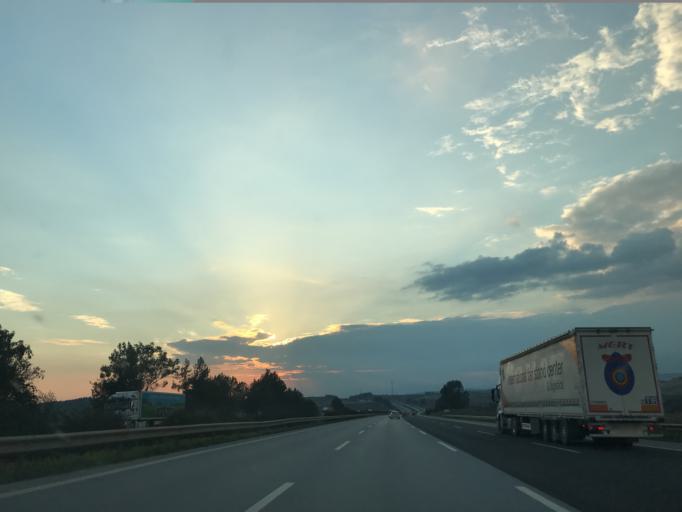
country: TR
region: Mersin
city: Yenice
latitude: 37.0207
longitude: 35.0321
